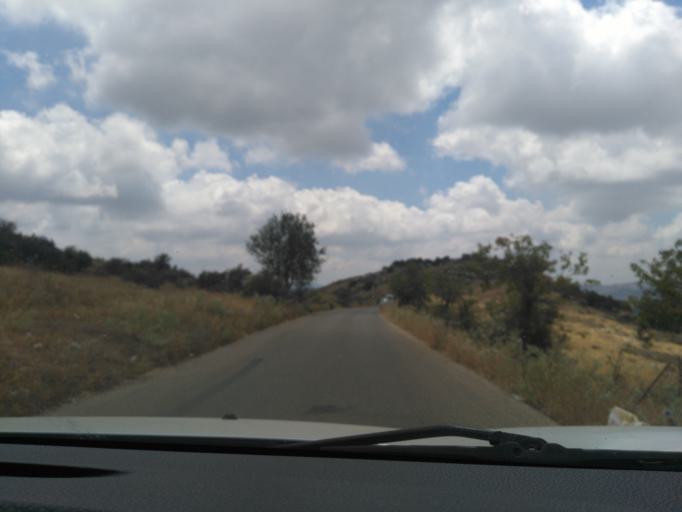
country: LB
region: Mont-Liban
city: Beit ed Dine
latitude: 33.6853
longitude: 35.6661
